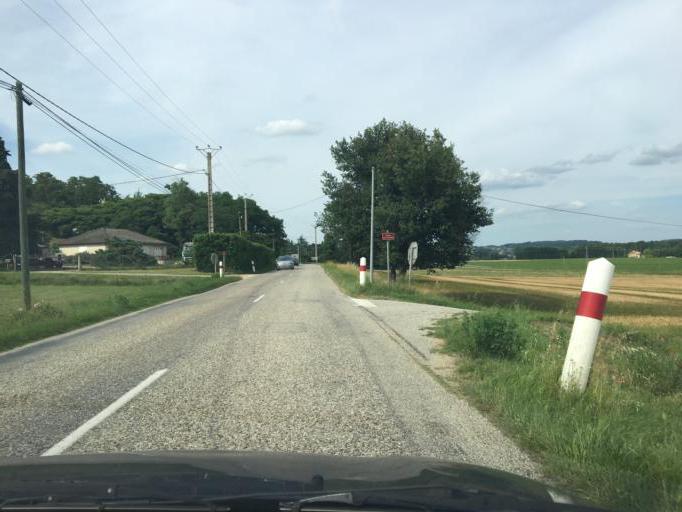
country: FR
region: Rhone-Alpes
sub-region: Departement de la Drome
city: Clerieux
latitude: 45.1015
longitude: 4.9479
